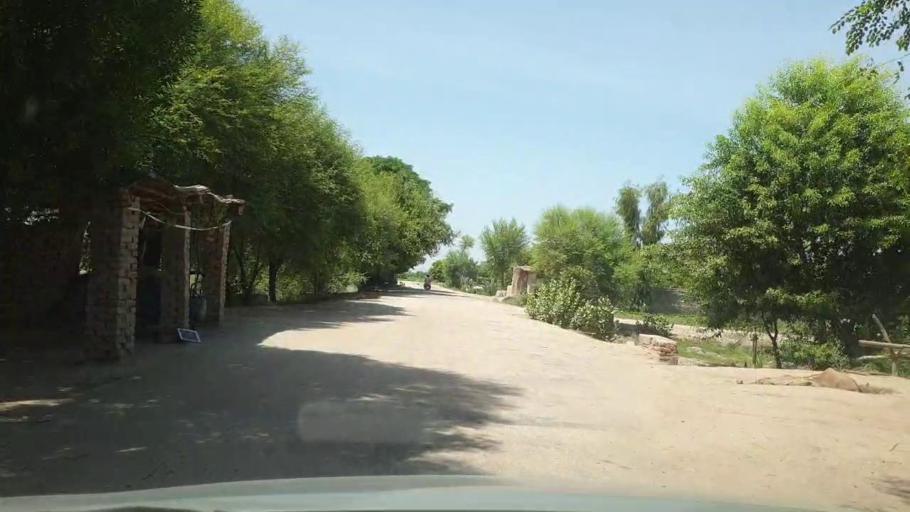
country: PK
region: Sindh
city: Pano Aqil
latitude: 27.6912
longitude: 69.1107
